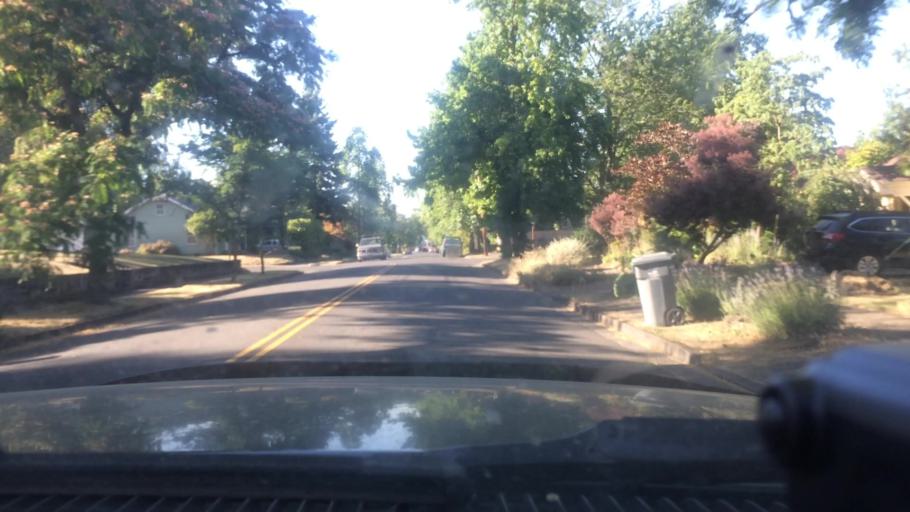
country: US
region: Oregon
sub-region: Lane County
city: Eugene
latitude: 44.0372
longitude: -123.1012
